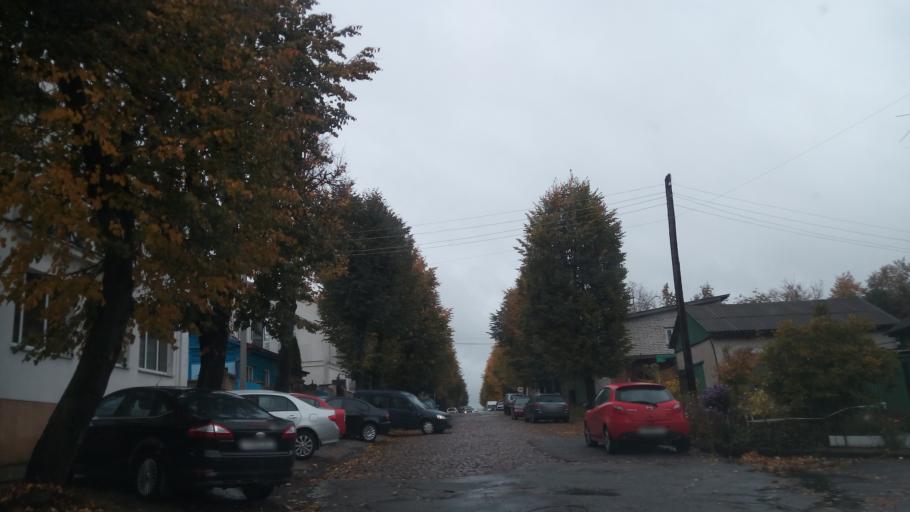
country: BY
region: Minsk
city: Minsk
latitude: 53.9444
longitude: 27.5963
